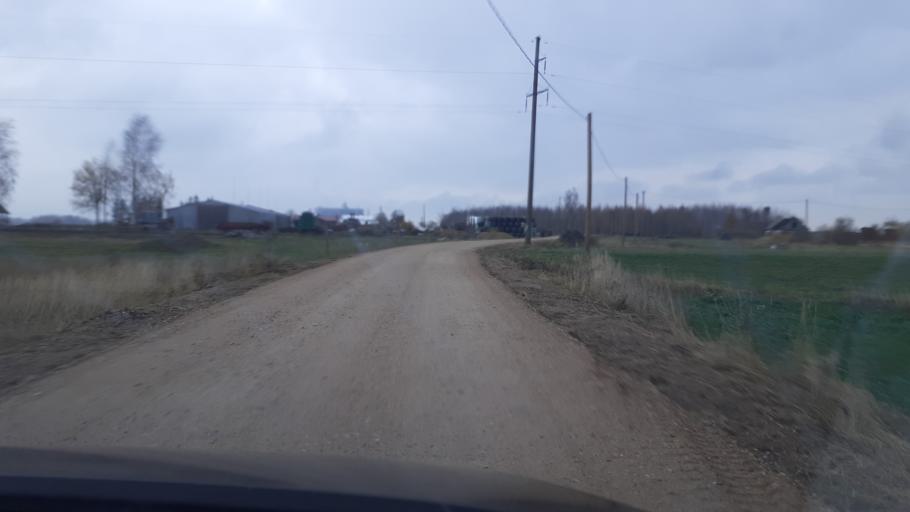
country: LV
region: Talsu Rajons
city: Sabile
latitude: 56.9393
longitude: 22.4192
